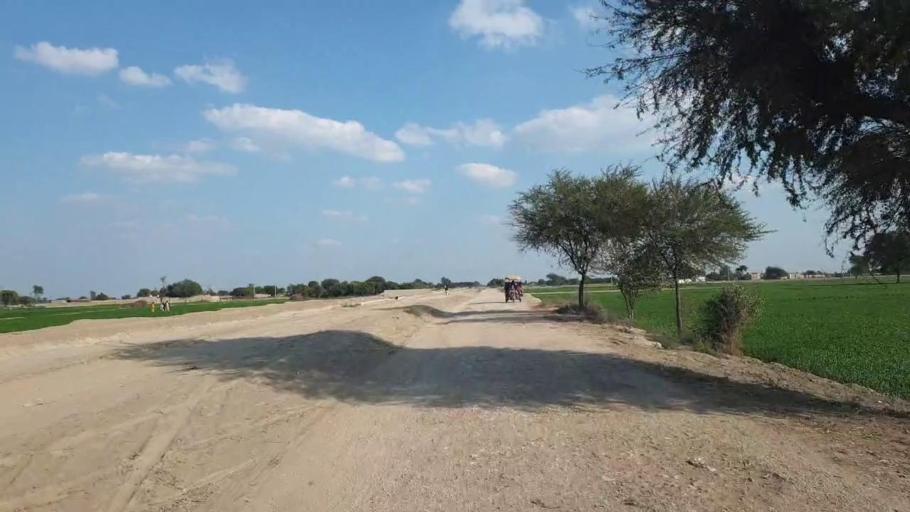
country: PK
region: Sindh
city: Shahpur Chakar
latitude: 26.1062
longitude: 68.5785
